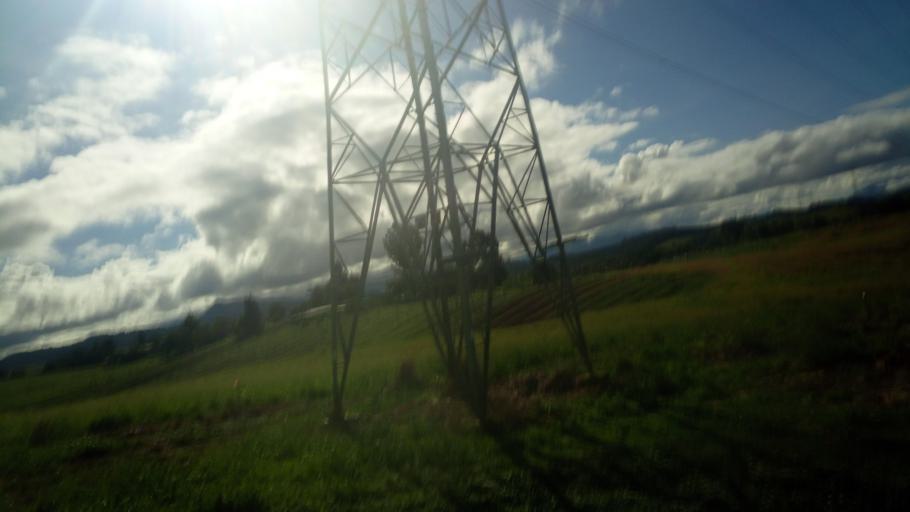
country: AU
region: Queensland
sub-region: Cassowary Coast
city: Innisfail
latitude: -17.5336
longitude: 145.9744
